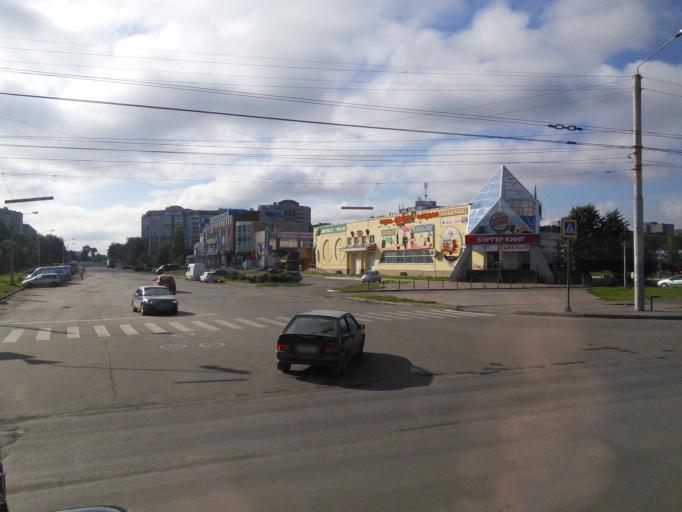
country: RU
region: Vologda
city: Vologda
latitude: 59.2059
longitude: 39.8387
